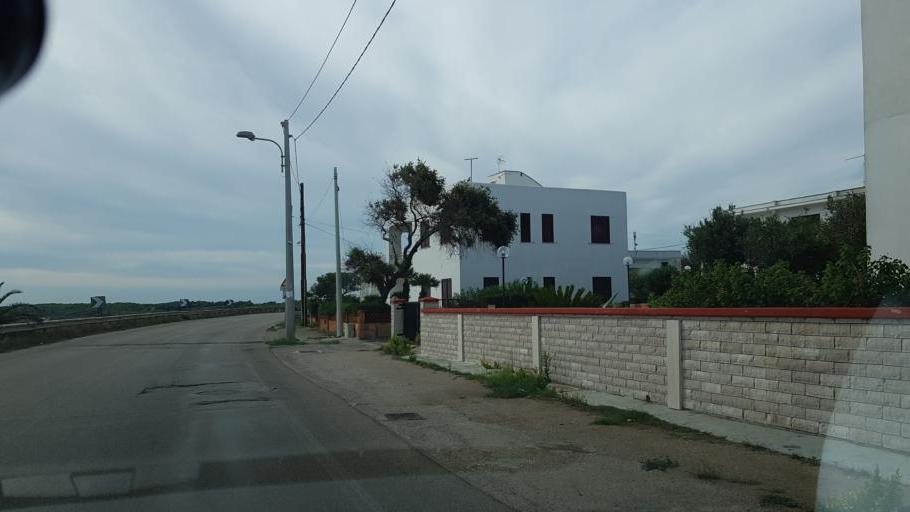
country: IT
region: Apulia
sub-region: Provincia di Lecce
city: Borgagne
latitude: 40.2800
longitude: 18.4313
